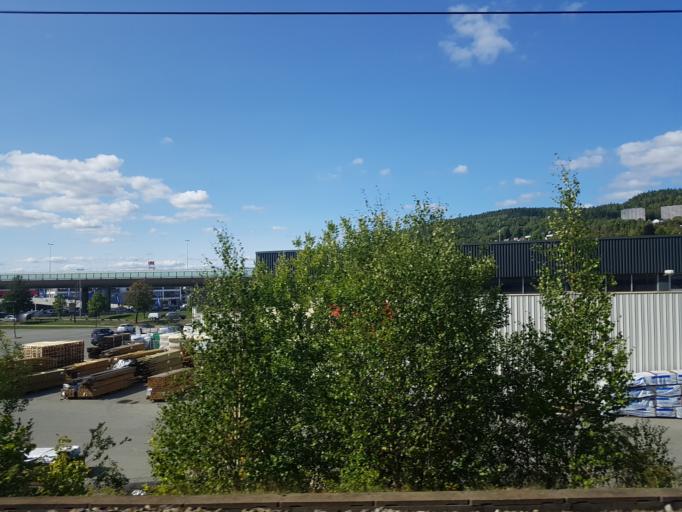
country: NO
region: Buskerud
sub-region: Drammen
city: Drammen
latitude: 59.7409
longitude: 10.2298
